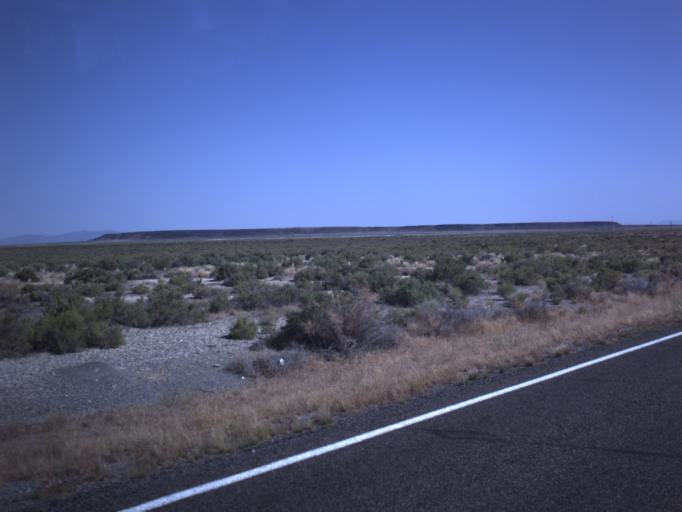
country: US
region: Utah
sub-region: Millard County
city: Delta
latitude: 39.1264
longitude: -112.7343
